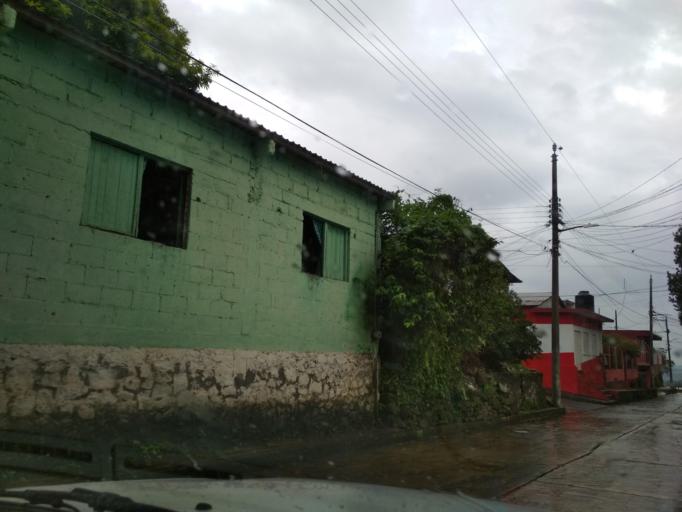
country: MX
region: Veracruz
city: San Andres Tuxtla
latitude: 18.4568
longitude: -95.2155
